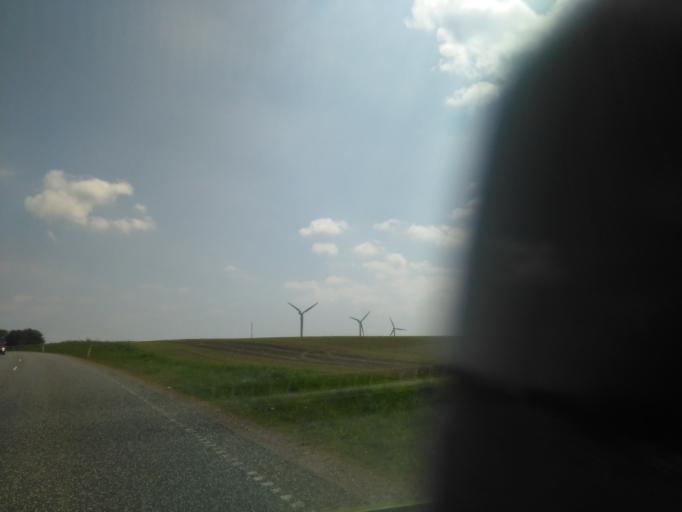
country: DK
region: Central Jutland
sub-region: Arhus Kommune
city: Solbjerg
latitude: 55.9873
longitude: 10.0314
